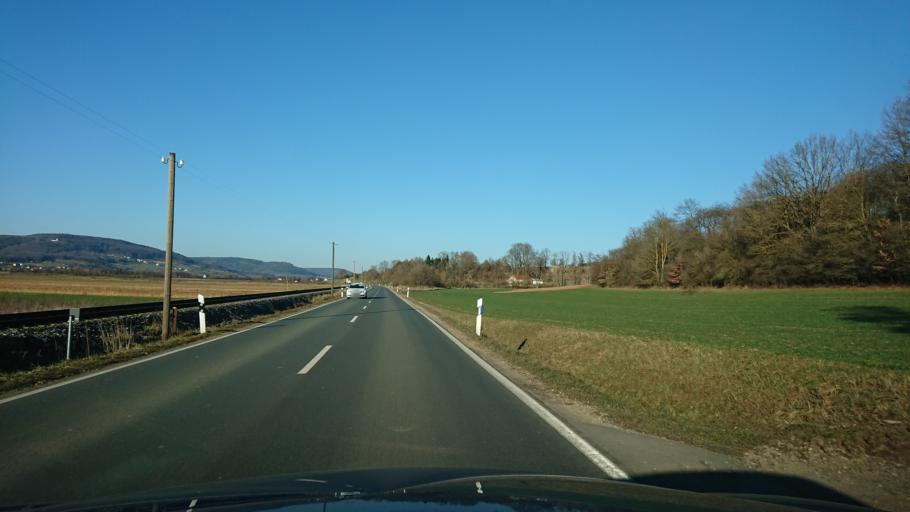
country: DE
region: Bavaria
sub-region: Upper Franconia
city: Wiesenthau
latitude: 49.7188
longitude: 11.1323
